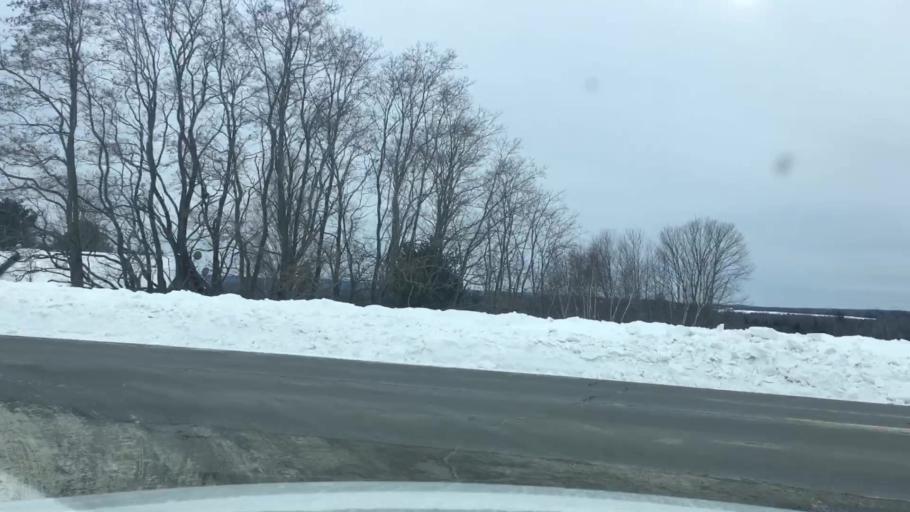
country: US
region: Maine
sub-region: Penobscot County
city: Charleston
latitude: 45.0290
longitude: -69.0318
